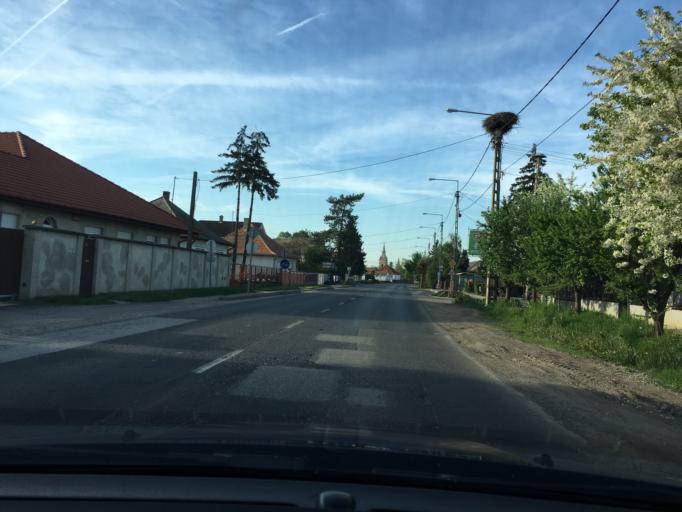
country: HU
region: Hajdu-Bihar
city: Berettyoujfalu
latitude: 47.1995
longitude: 21.5381
